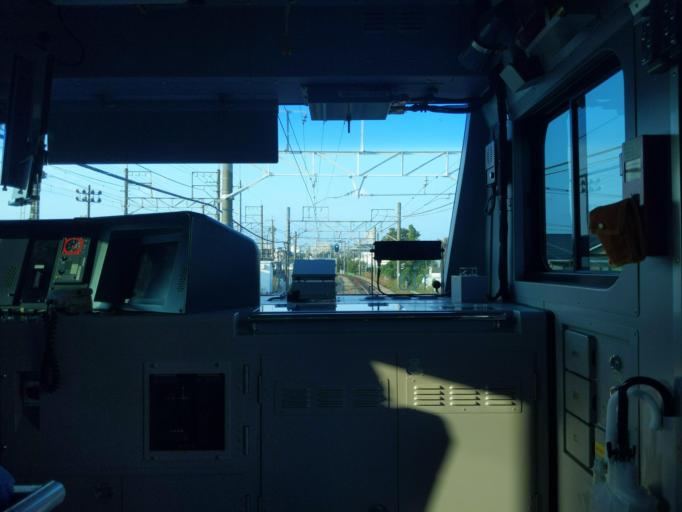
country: JP
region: Tokyo
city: Kokubunji
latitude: 35.6556
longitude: 139.4831
